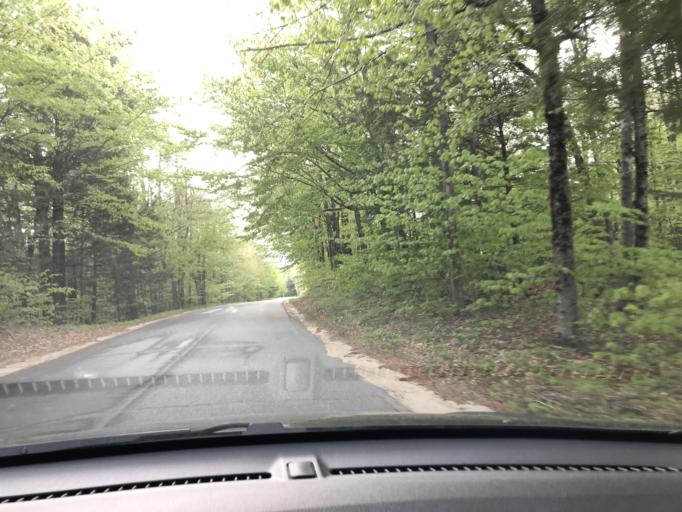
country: US
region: New Hampshire
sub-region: Merrimack County
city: New London
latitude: 43.4171
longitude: -71.9994
